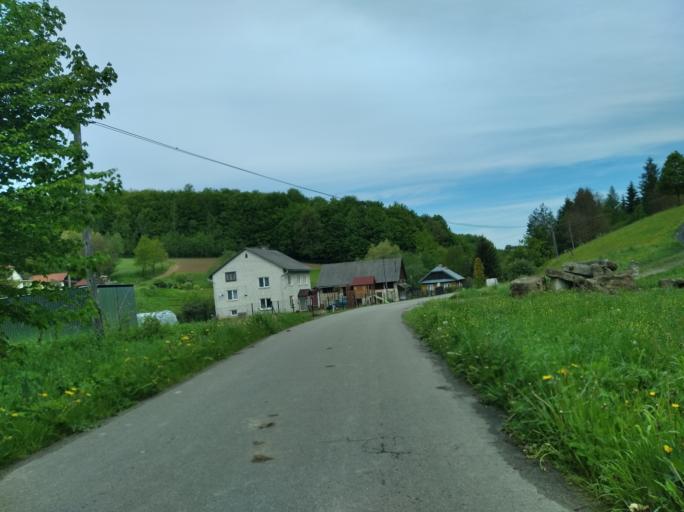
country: PL
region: Subcarpathian Voivodeship
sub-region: Powiat strzyzowski
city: Strzyzow
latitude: 49.9190
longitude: 21.7554
